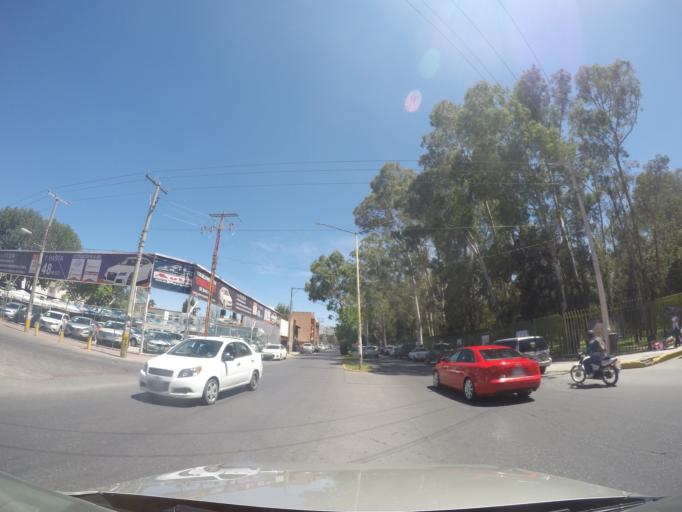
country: MX
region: San Luis Potosi
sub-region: San Luis Potosi
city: San Luis Potosi
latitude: 22.1505
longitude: -101.0151
